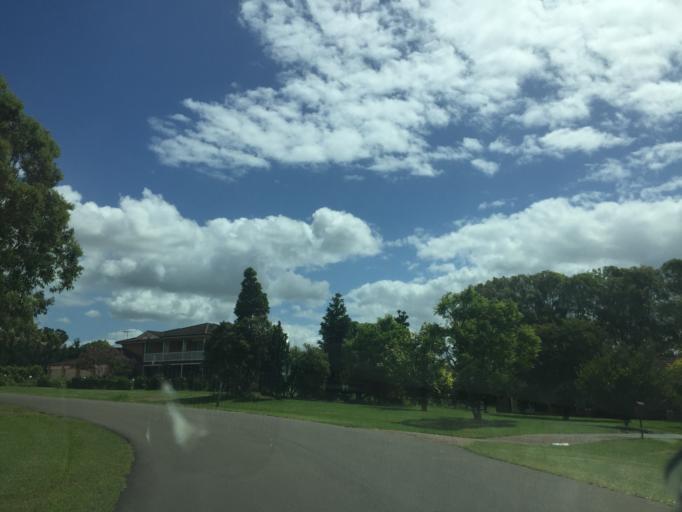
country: AU
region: New South Wales
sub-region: Penrith Municipality
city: Kingswood Park
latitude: -33.7946
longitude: 150.7471
